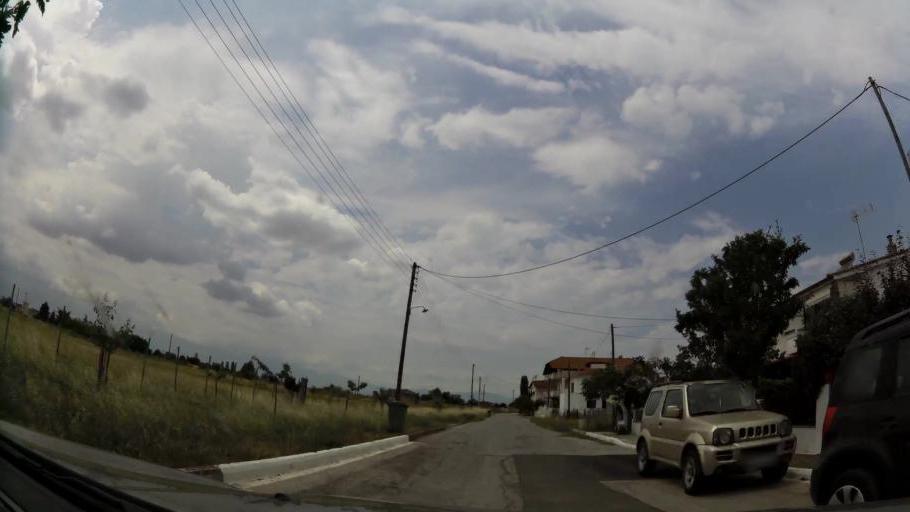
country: GR
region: Central Macedonia
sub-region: Nomos Pierias
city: Kallithea
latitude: 40.2732
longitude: 22.5718
